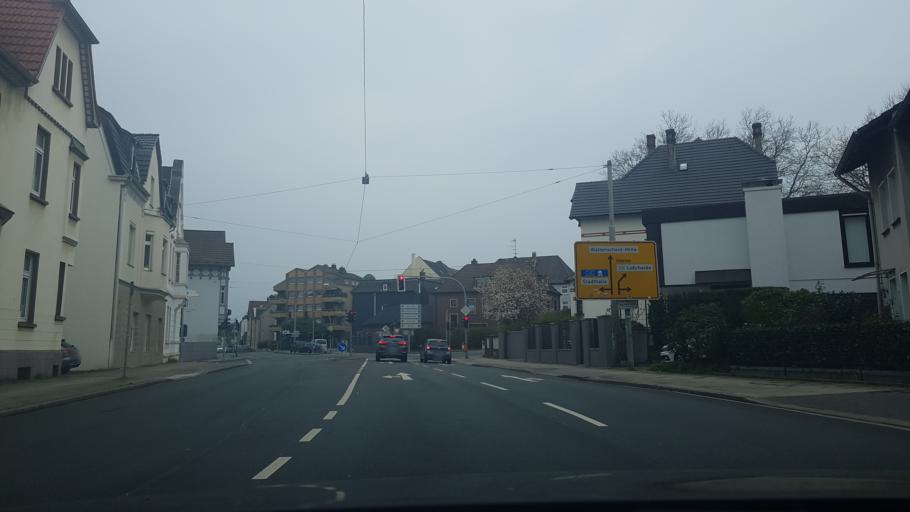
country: DE
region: North Rhine-Westphalia
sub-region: Regierungsbezirk Munster
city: Gelsenkirchen
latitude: 51.4769
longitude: 7.1445
